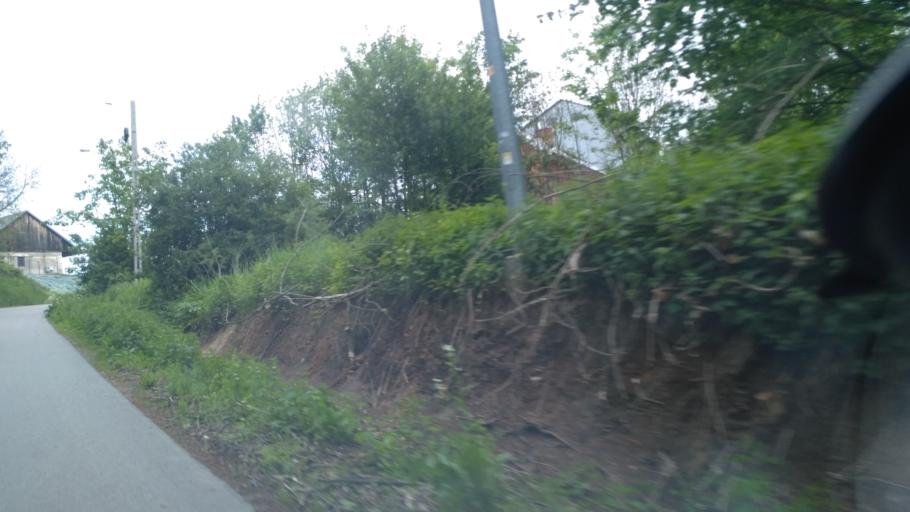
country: PL
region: Subcarpathian Voivodeship
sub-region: Powiat przeworski
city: Jawornik Polski
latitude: 49.8363
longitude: 22.2918
